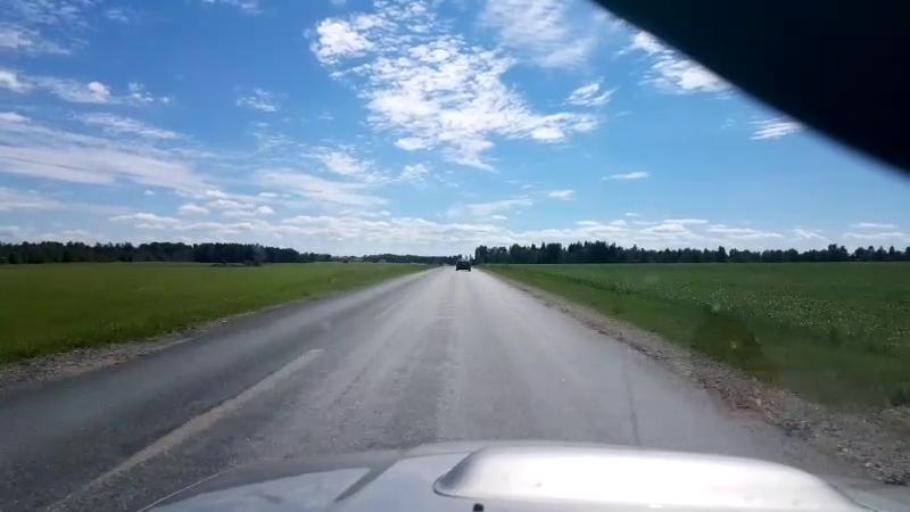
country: EE
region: Jogevamaa
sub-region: Jogeva linn
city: Jogeva
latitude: 58.8323
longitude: 26.2879
